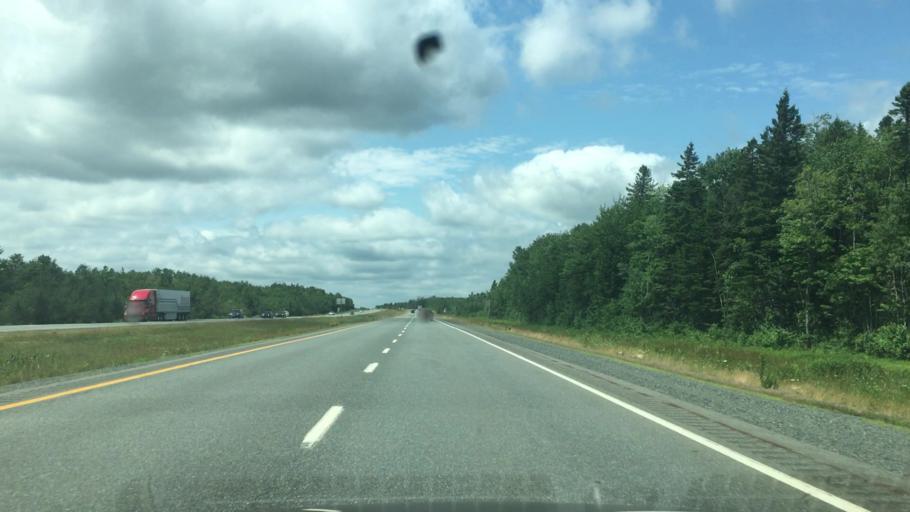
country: CA
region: Nova Scotia
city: Oxford
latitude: 45.7141
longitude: -63.9360
